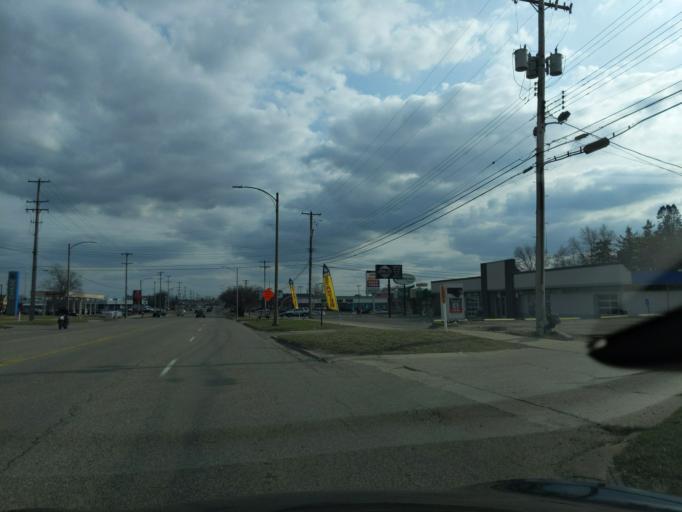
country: US
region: Michigan
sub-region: Ingham County
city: Holt
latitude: 42.6713
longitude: -84.5383
